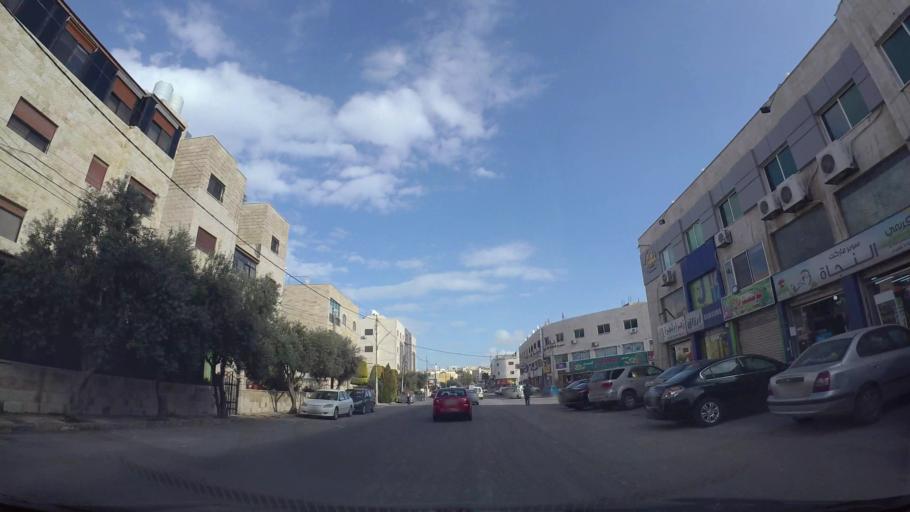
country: JO
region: Amman
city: Umm as Summaq
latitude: 31.9002
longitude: 35.8559
